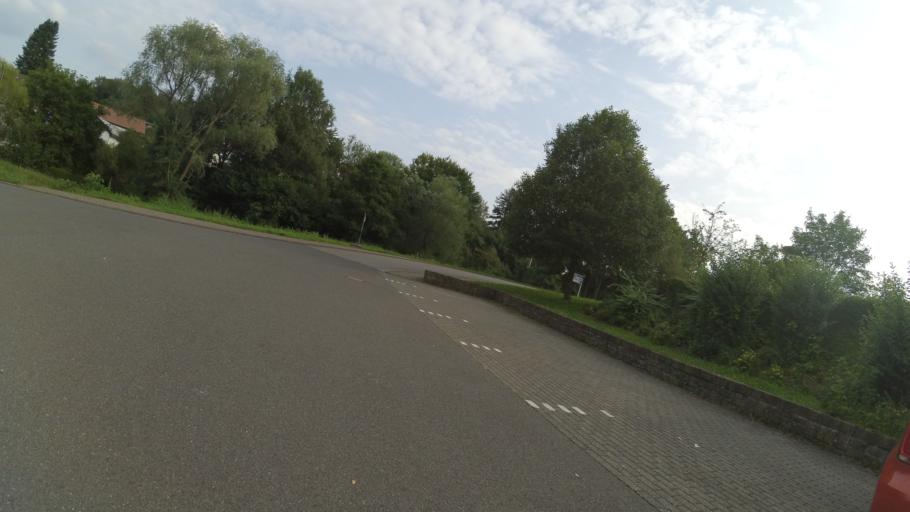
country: DE
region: Rheinland-Pfalz
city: Zerf
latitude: 49.6008
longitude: 6.6858
